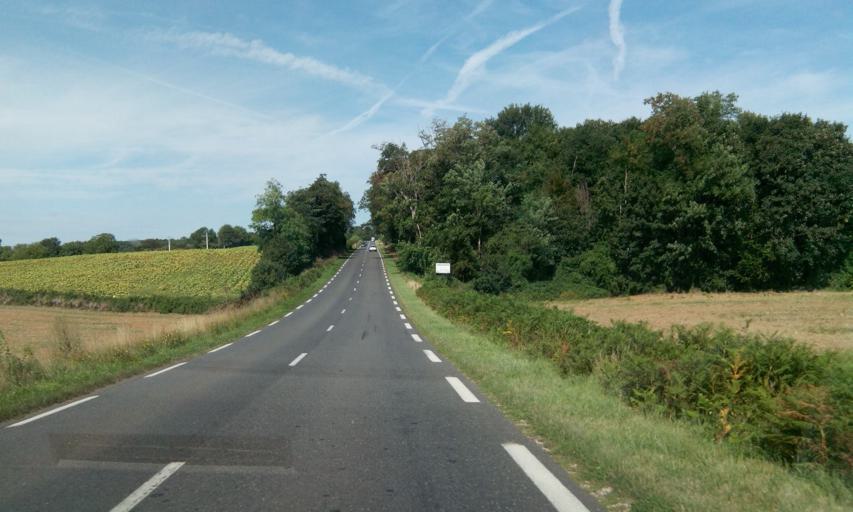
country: FR
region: Poitou-Charentes
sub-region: Departement de la Vienne
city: Savigne
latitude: 46.1575
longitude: 0.3577
